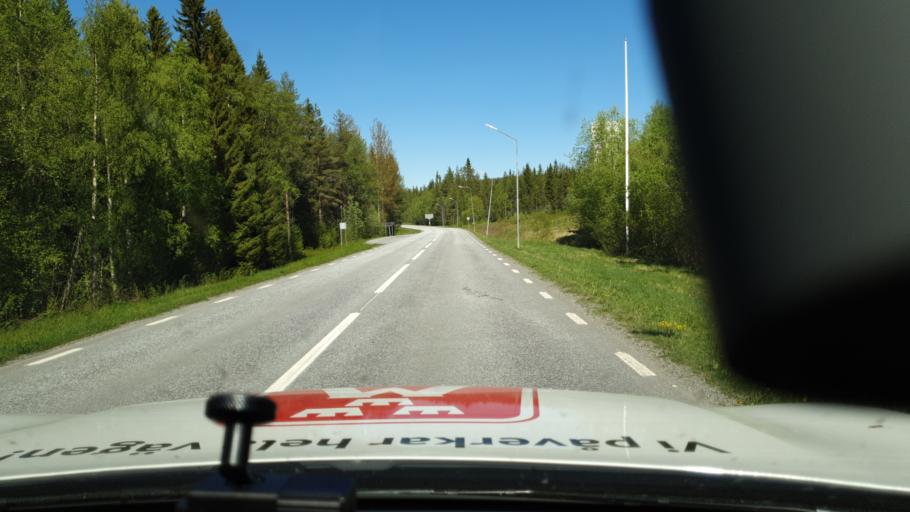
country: SE
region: Vaesterbotten
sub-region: Storumans Kommun
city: Storuman
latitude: 65.1122
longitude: 17.1214
